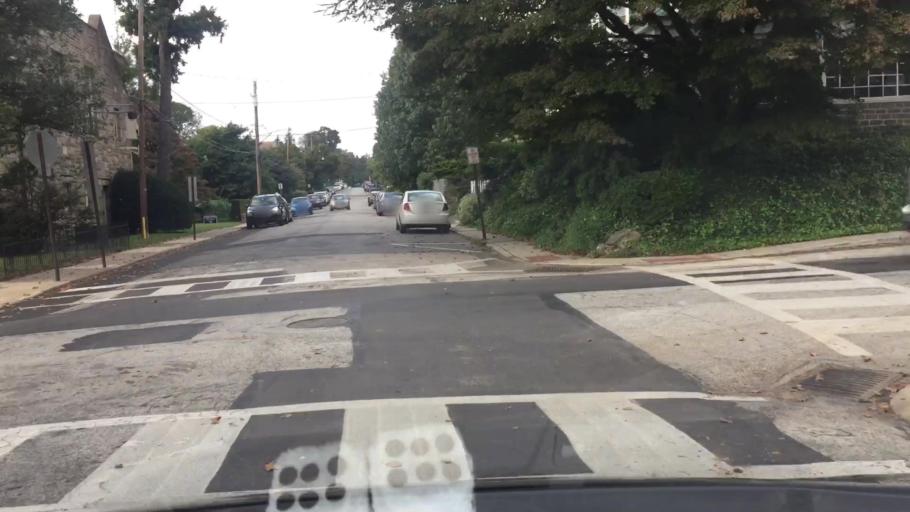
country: US
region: Pennsylvania
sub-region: Montgomery County
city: Narberth
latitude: 40.0073
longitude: -75.2589
